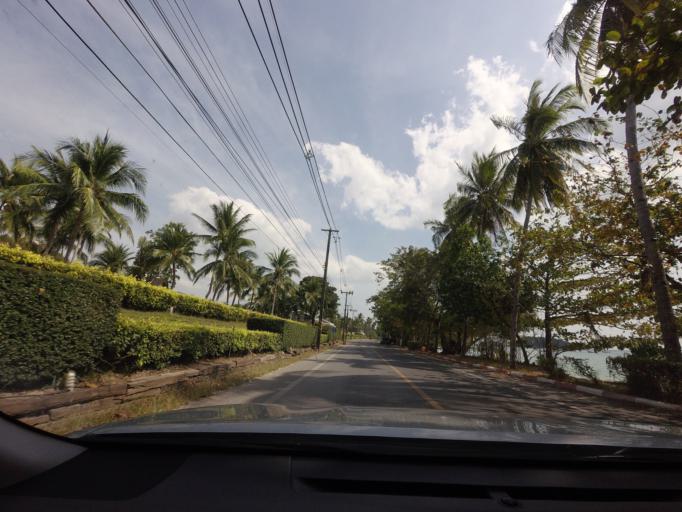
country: TH
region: Phangnga
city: Ban Ao Nang
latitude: 8.0631
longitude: 98.7459
